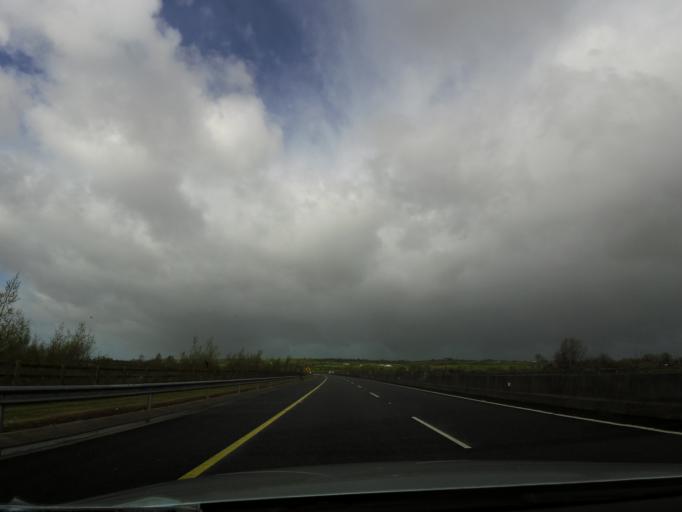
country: IE
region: Munster
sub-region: North Tipperary
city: Nenagh
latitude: 52.8452
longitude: -8.2498
